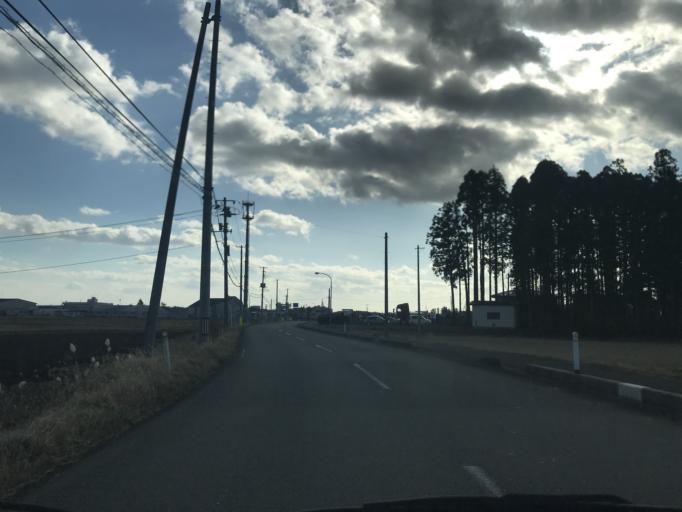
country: JP
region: Iwate
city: Ichinoseki
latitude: 38.7576
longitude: 141.0624
